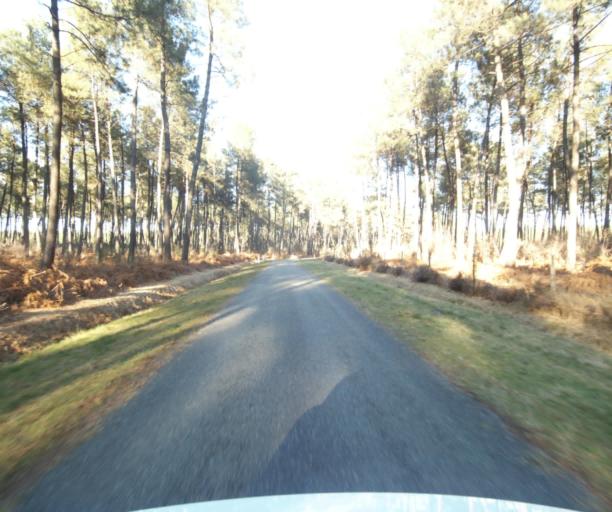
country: FR
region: Aquitaine
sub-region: Departement des Landes
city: Gabarret
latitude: 44.1486
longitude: -0.0751
